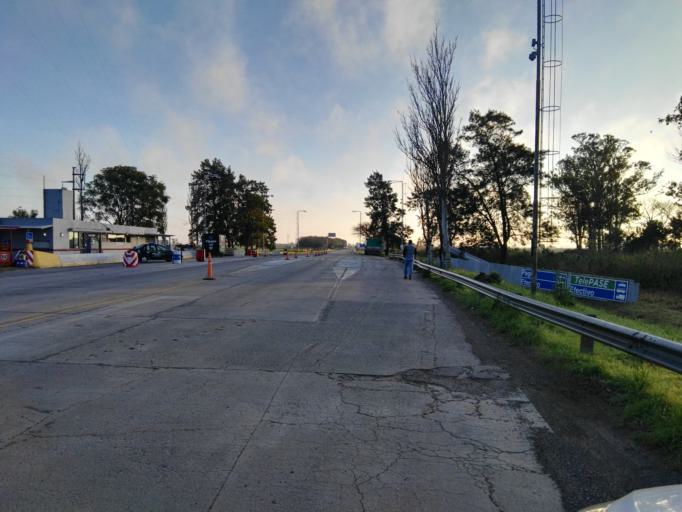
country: AR
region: Santa Fe
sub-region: Departamento de San Justo
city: San Justo
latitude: -30.9913
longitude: -60.6833
